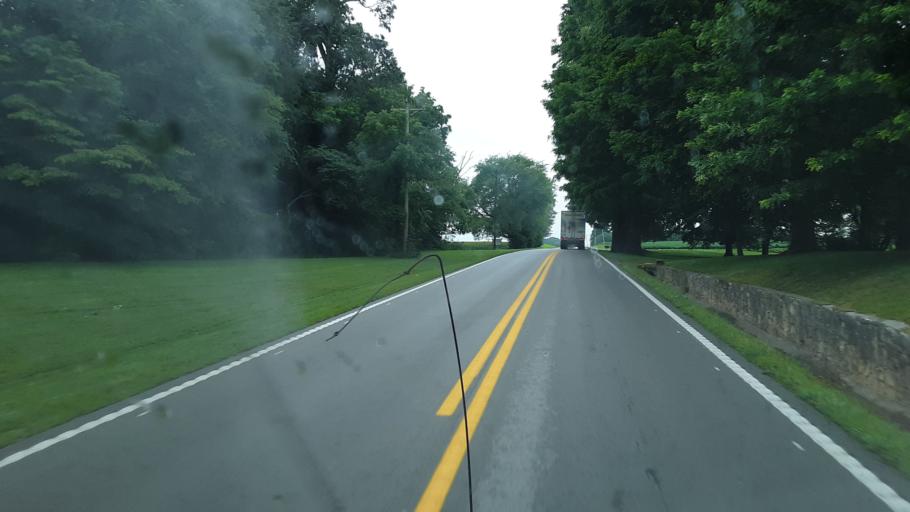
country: US
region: Kentucky
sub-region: Todd County
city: Elkton
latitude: 36.7395
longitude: -87.0624
